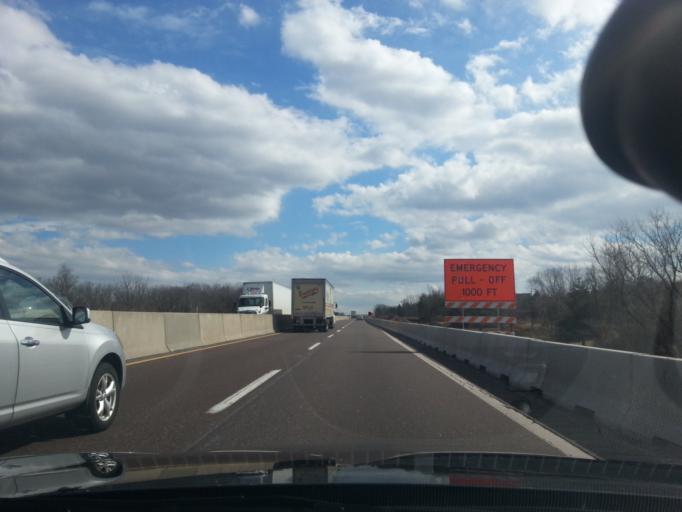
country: US
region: Pennsylvania
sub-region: Montgomery County
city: Kulpsville
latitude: 40.2179
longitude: -75.3284
